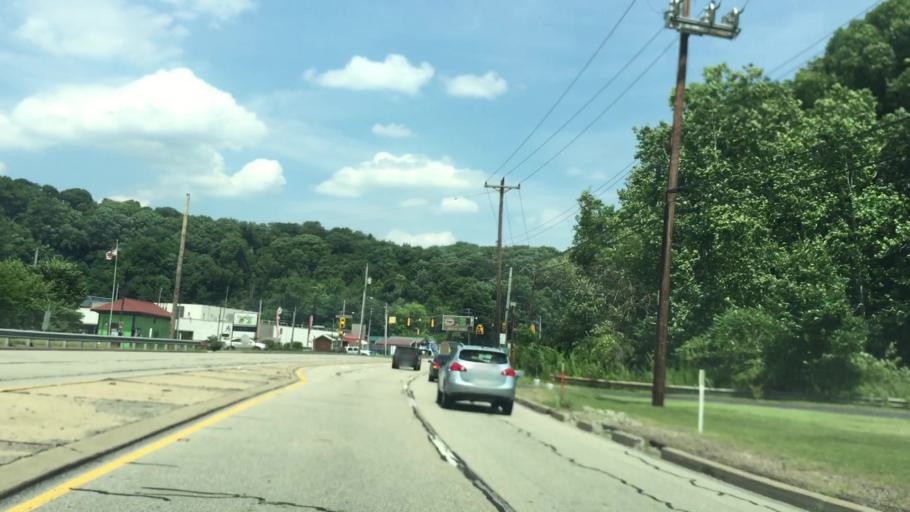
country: US
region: Pennsylvania
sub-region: Allegheny County
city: Glenshaw
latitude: 40.5412
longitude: -79.9638
